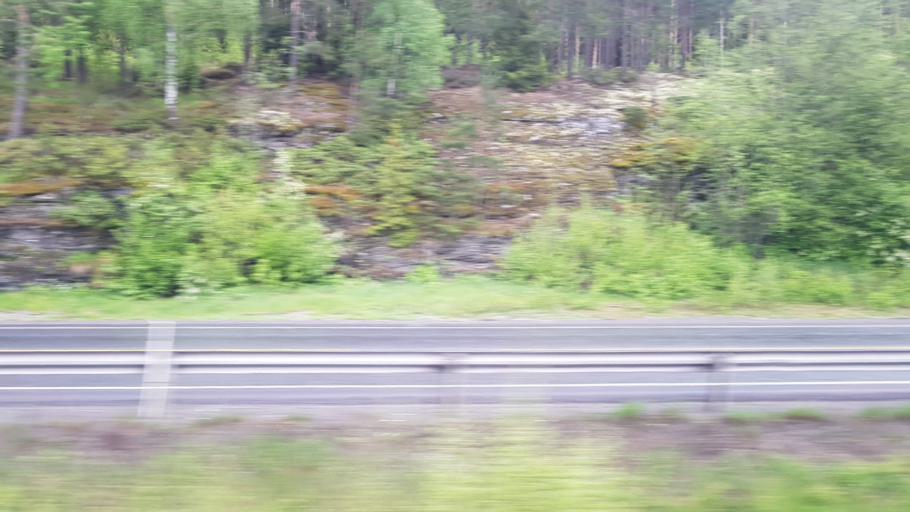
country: NO
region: Oppland
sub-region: Ringebu
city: Ringebu
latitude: 61.5360
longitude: 10.1130
